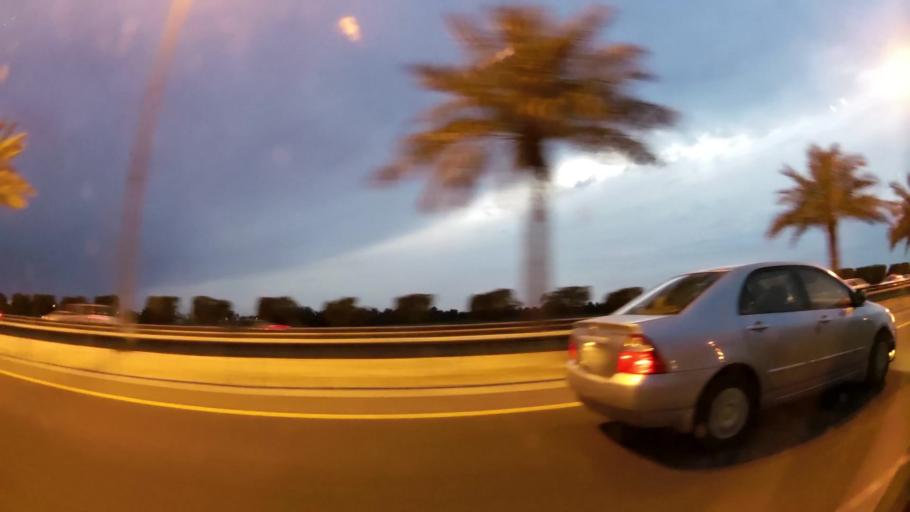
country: BH
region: Central Governorate
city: Madinat Hamad
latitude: 26.1547
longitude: 50.5069
